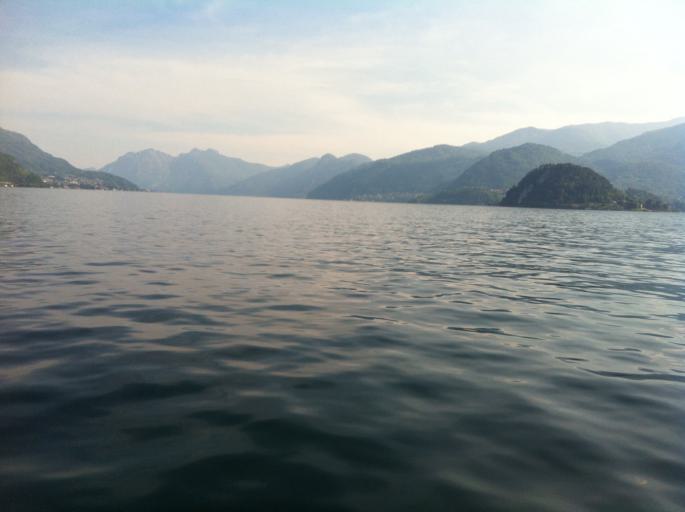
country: IT
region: Lombardy
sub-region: Provincia di Lecco
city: Varenna
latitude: 46.0083
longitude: 9.2741
